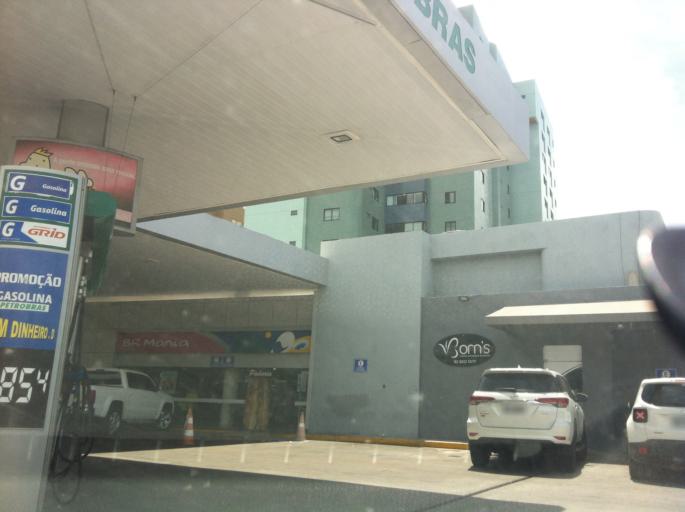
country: BR
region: Alagoas
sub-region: Maceio
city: Maceio
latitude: -9.6704
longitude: -35.7166
